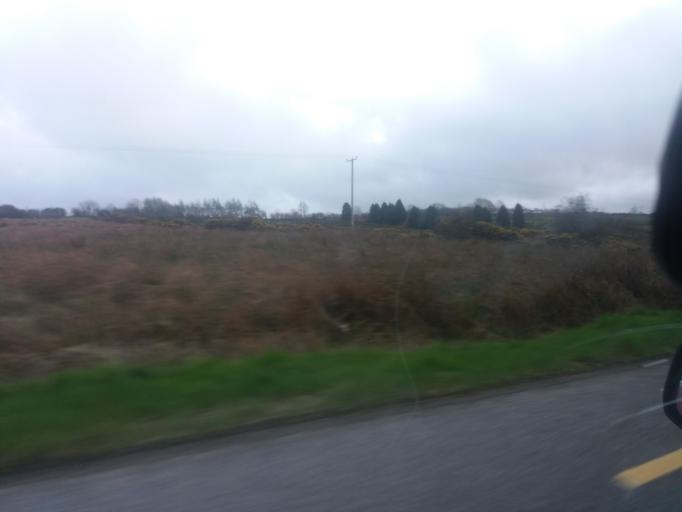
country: IE
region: Munster
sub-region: County Limerick
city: Newcastle West
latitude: 52.4107
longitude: -9.1563
